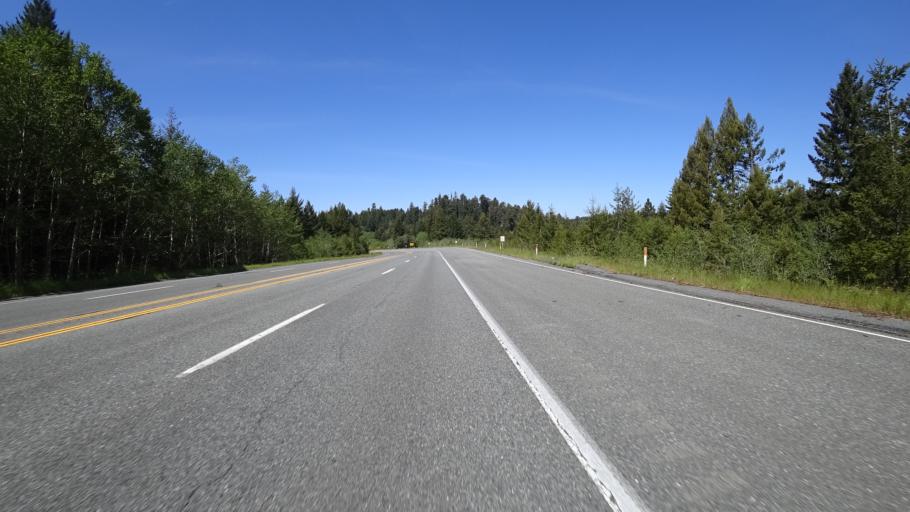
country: US
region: California
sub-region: Humboldt County
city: Westhaven-Moonstone
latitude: 41.3593
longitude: -123.9997
